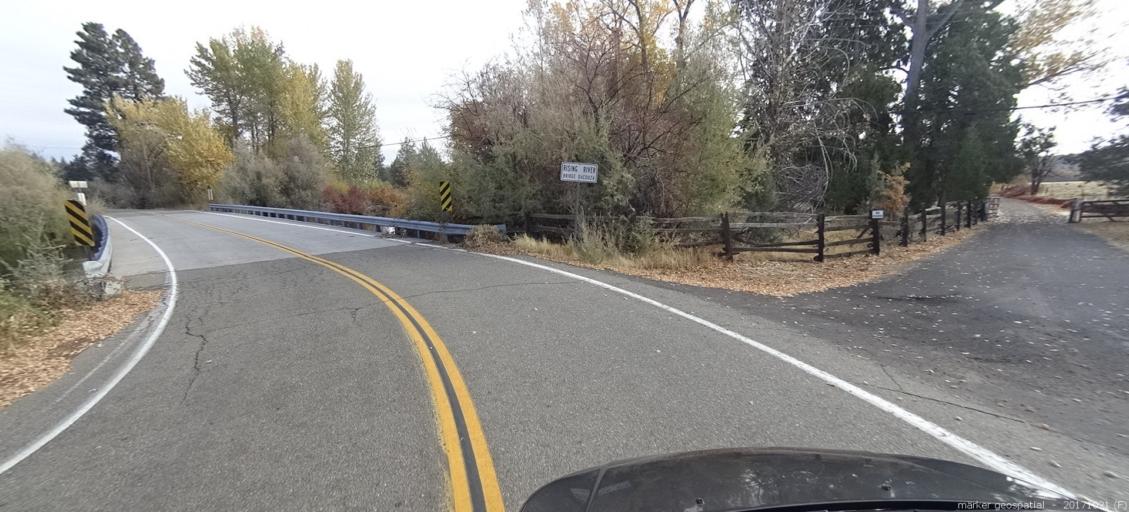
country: US
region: California
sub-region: Shasta County
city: Burney
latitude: 40.8990
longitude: -121.5476
